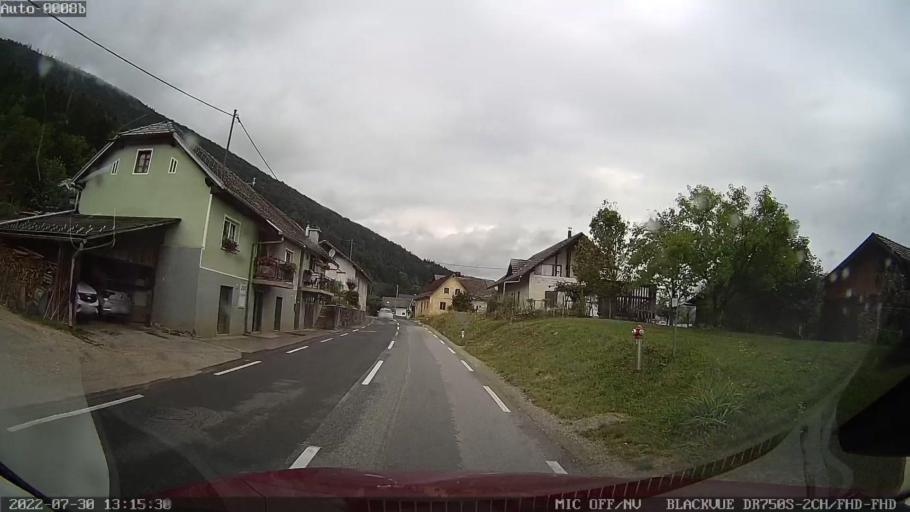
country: SI
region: Dolenjske Toplice
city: Dolenjske Toplice
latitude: 45.7399
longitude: 15.0424
